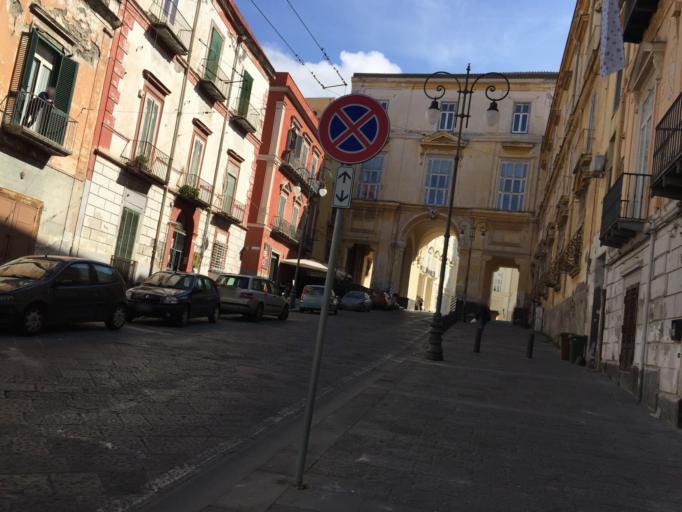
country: IT
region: Campania
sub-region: Provincia di Napoli
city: Portici
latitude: 40.8119
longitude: 14.3417
